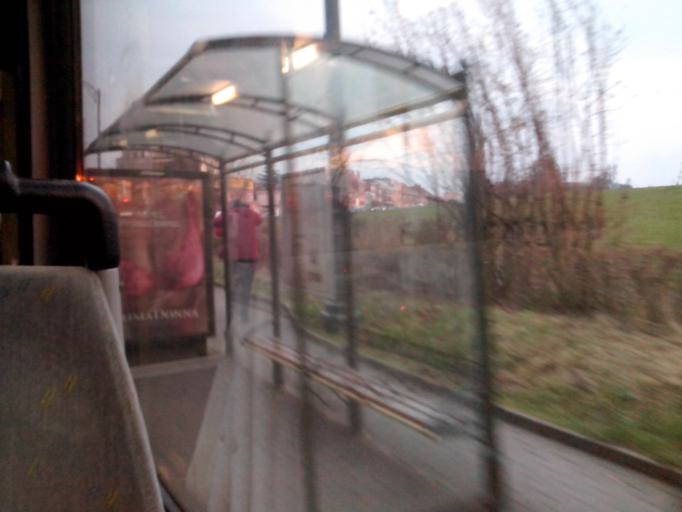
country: BE
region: Flanders
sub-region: Provincie Vlaams-Brabant
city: Wemmel
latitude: 50.8717
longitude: 4.2972
